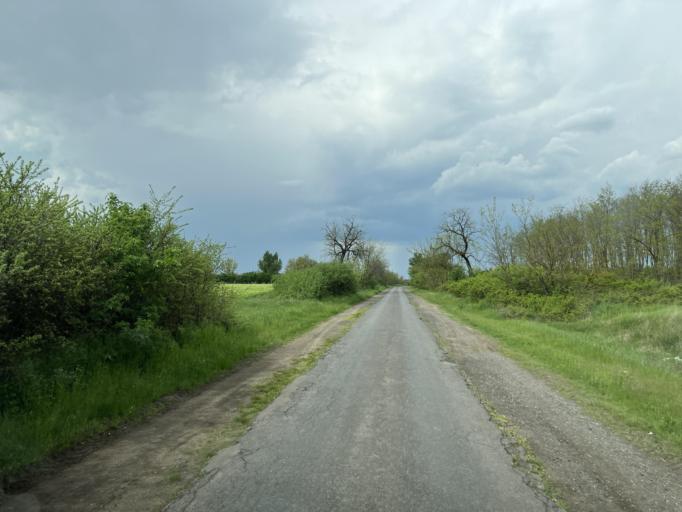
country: HU
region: Pest
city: Nagykoros
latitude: 46.9939
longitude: 19.8024
